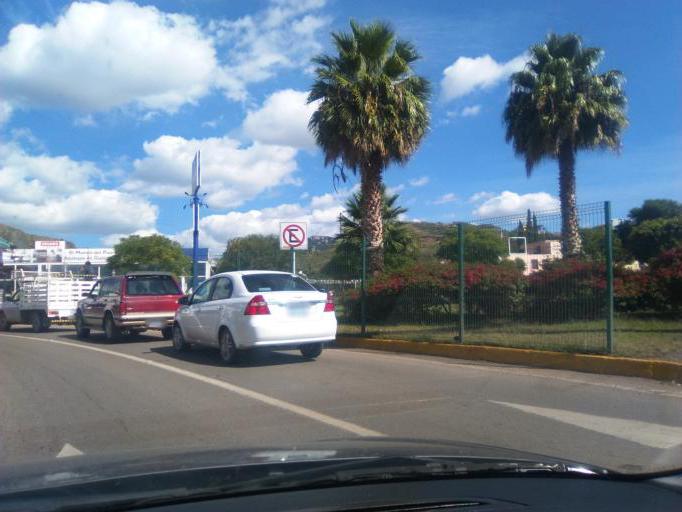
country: MX
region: Guanajuato
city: Marfil
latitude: 20.9861
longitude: -101.2854
